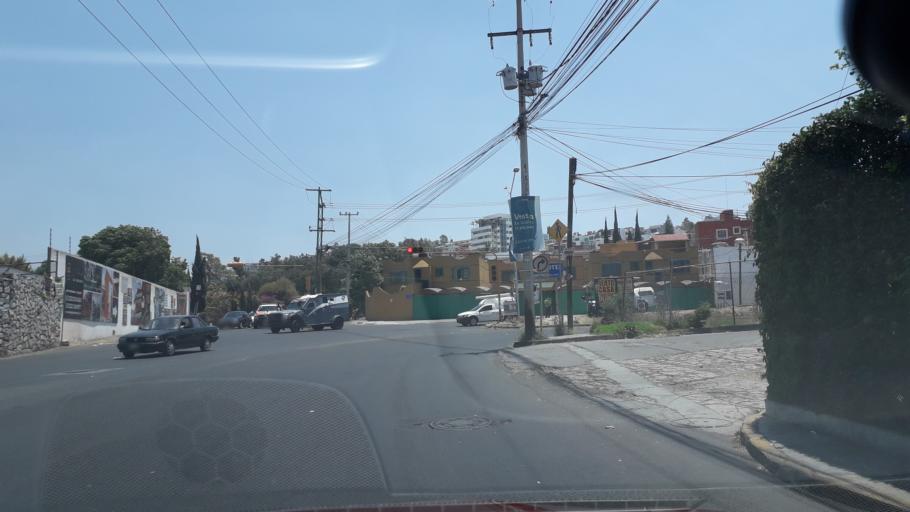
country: MX
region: Puebla
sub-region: Puebla
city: Galaxia la Calera
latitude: 19.0090
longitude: -98.1805
